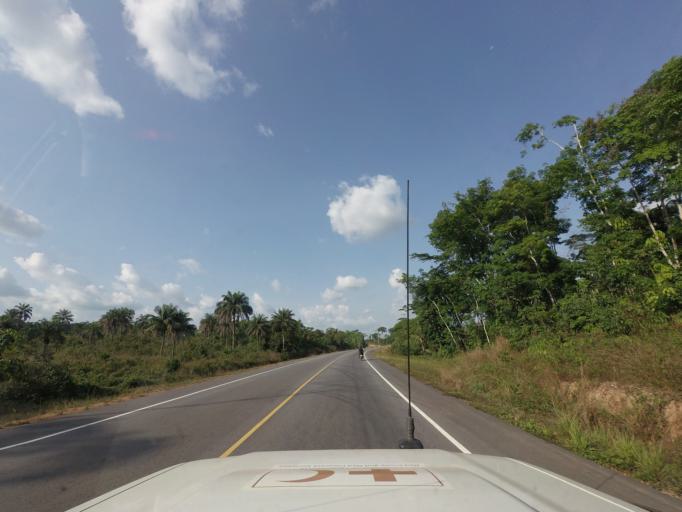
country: LR
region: Bong
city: Gbarnga
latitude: 6.9289
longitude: -9.6420
